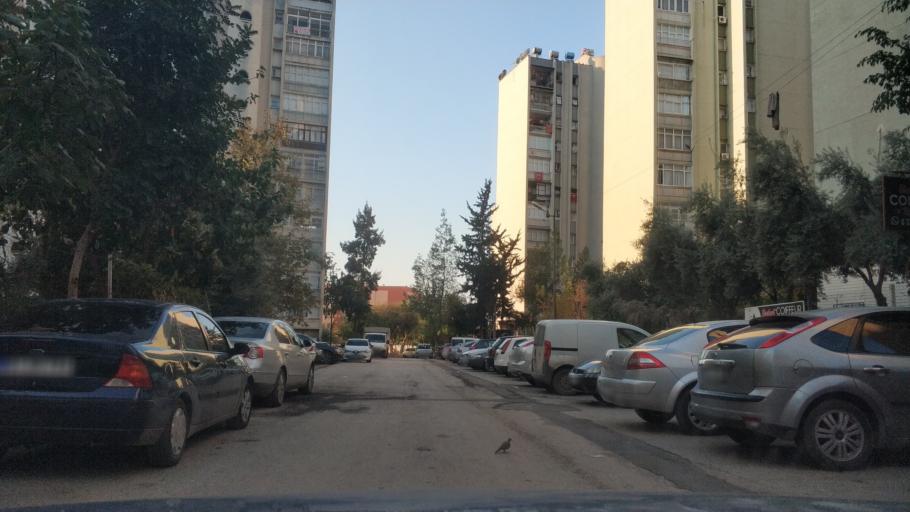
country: TR
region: Adana
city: Yuregir
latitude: 37.0053
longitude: 35.3623
